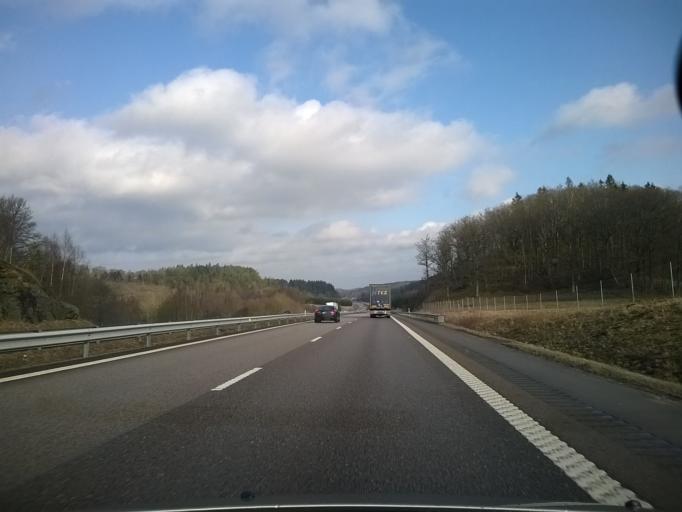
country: SE
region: Vaestra Goetaland
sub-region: Uddevalla Kommun
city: Ljungskile
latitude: 58.2593
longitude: 11.8991
